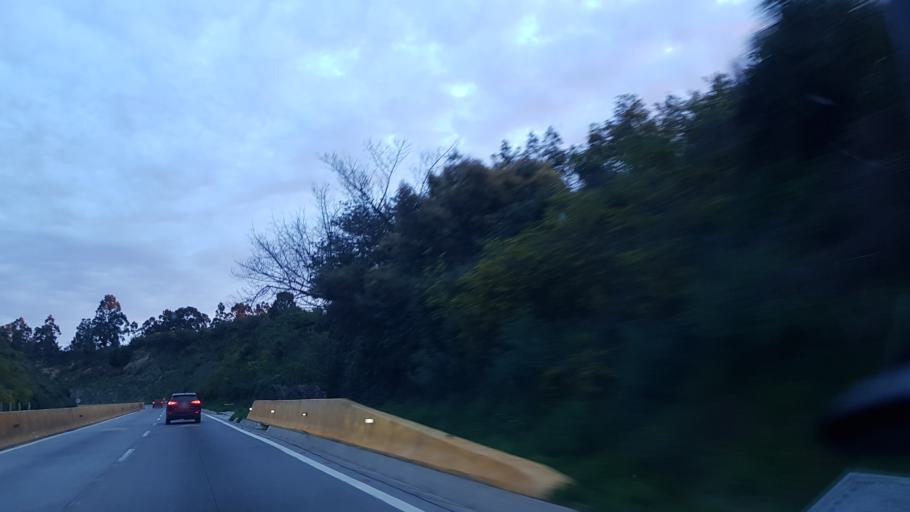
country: CL
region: Valparaiso
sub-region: Provincia de Valparaiso
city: Valparaiso
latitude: -33.0632
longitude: -71.6417
